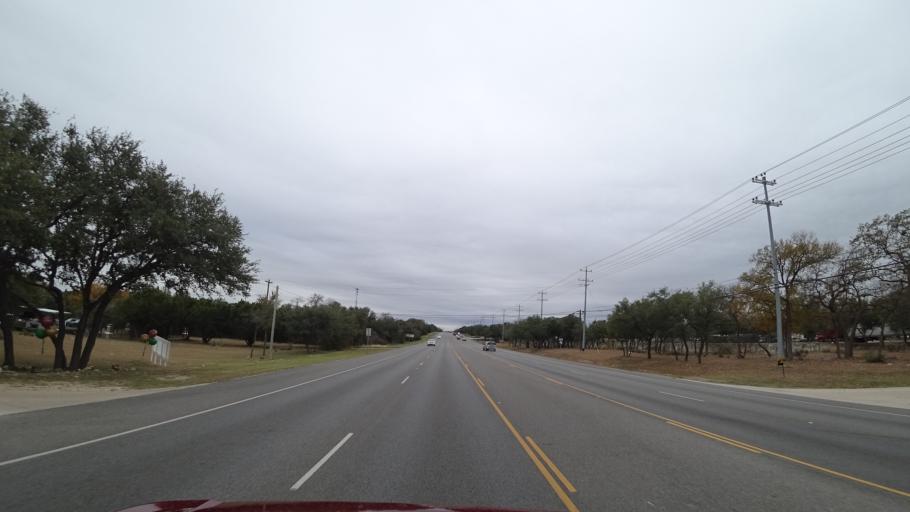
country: US
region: Texas
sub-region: Williamson County
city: Anderson Mill
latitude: 30.4154
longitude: -97.8480
